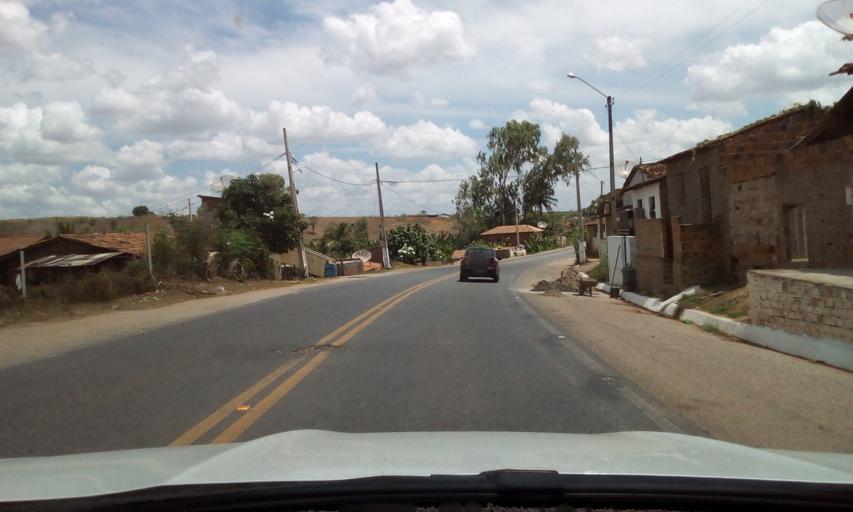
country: BR
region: Paraiba
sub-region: Guarabira
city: Guarabira
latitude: -6.8938
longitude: -35.5222
